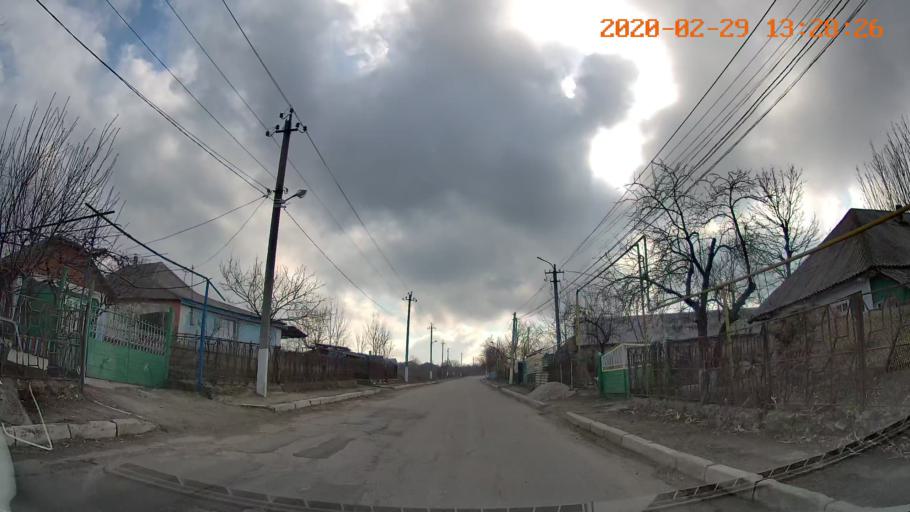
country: MD
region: Telenesti
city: Camenca
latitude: 47.9054
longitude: 28.6423
